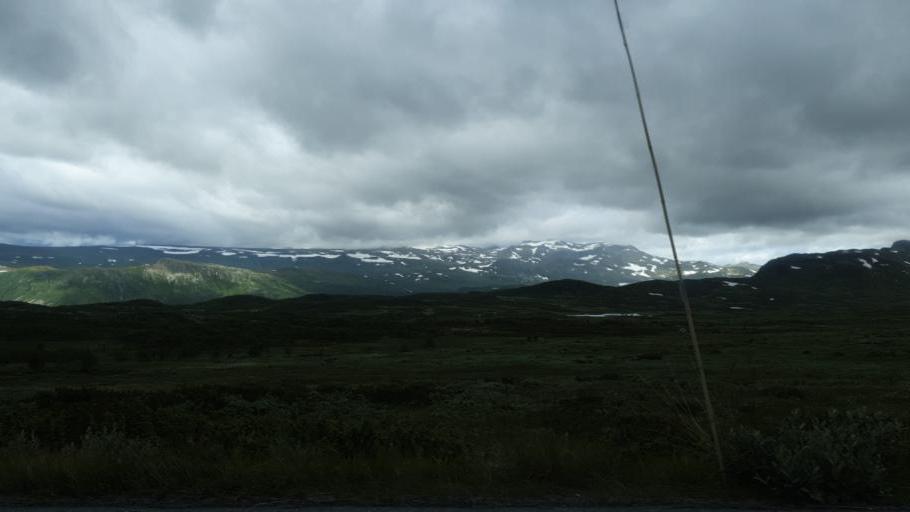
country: NO
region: Oppland
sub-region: Vestre Slidre
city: Slidre
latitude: 61.2705
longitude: 8.8625
